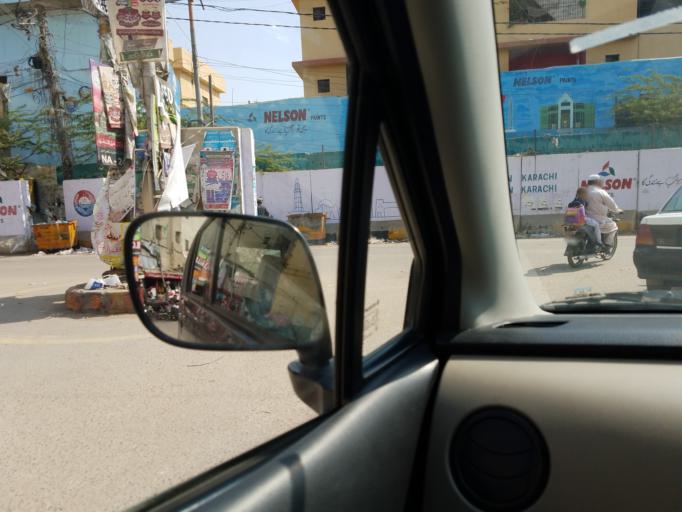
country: PK
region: Sindh
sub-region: Karachi District
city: Karachi
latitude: 24.8904
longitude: 67.0521
